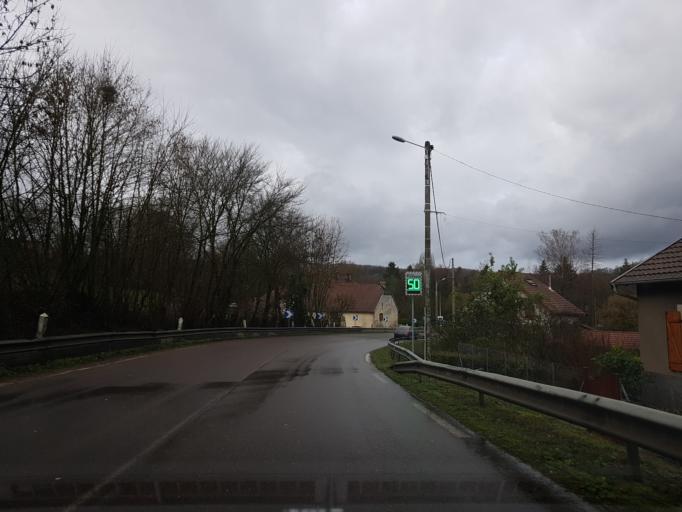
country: FR
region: Franche-Comte
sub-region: Departement de la Haute-Saone
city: Magny-Vernois
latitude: 47.6675
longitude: 6.3774
